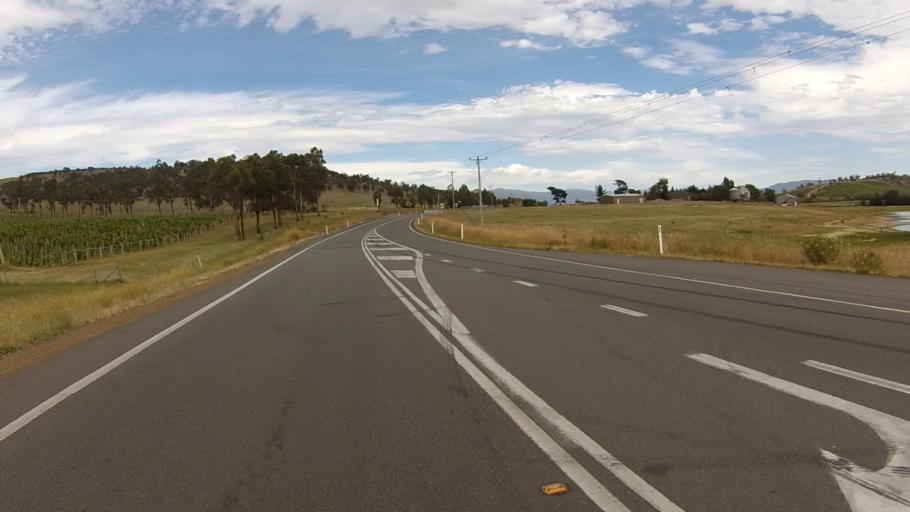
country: AU
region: Tasmania
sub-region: Brighton
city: Old Beach
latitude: -42.6904
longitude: 147.3433
